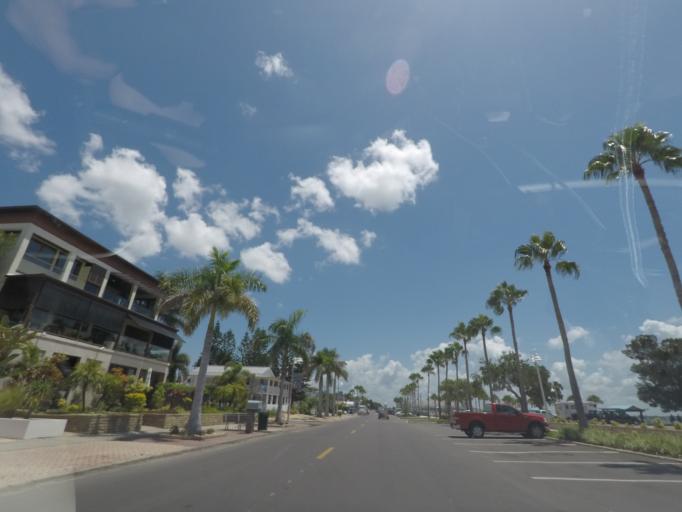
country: US
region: Florida
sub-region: Pinellas County
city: Gulfport
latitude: 27.7378
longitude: -82.7099
